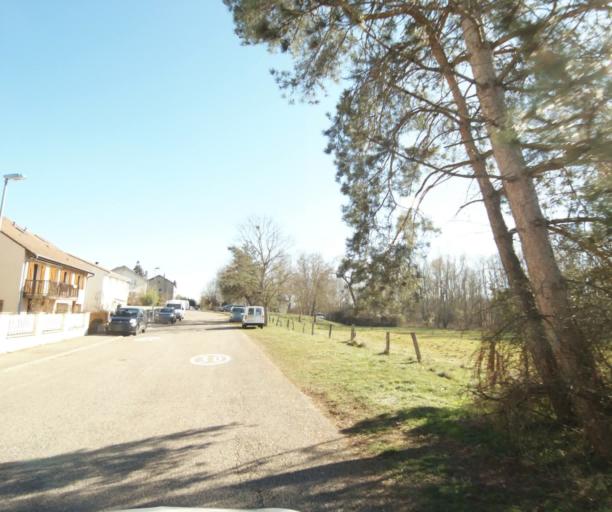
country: FR
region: Lorraine
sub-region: Departement de Meurthe-et-Moselle
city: Tomblaine
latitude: 48.6756
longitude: 6.2167
